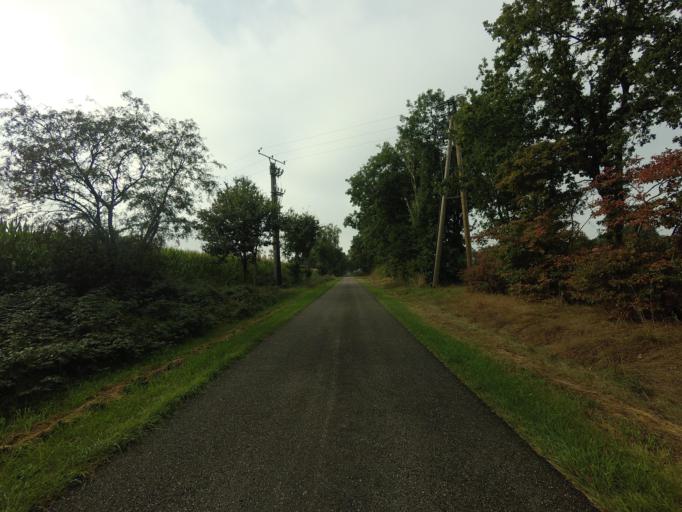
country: DE
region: Lower Saxony
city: Wielen
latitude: 52.5117
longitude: 6.7280
